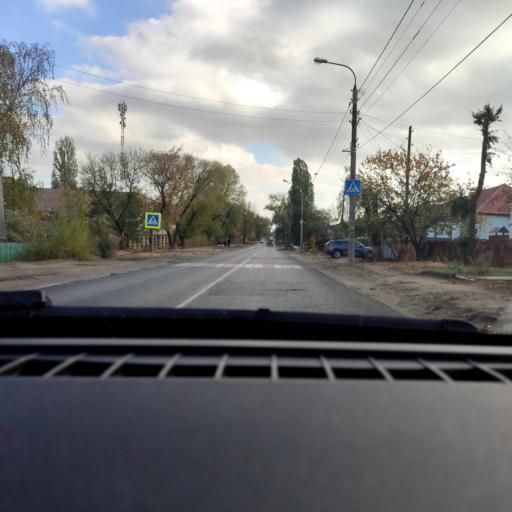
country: RU
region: Voronezj
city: Maslovka
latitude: 51.6103
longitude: 39.2277
